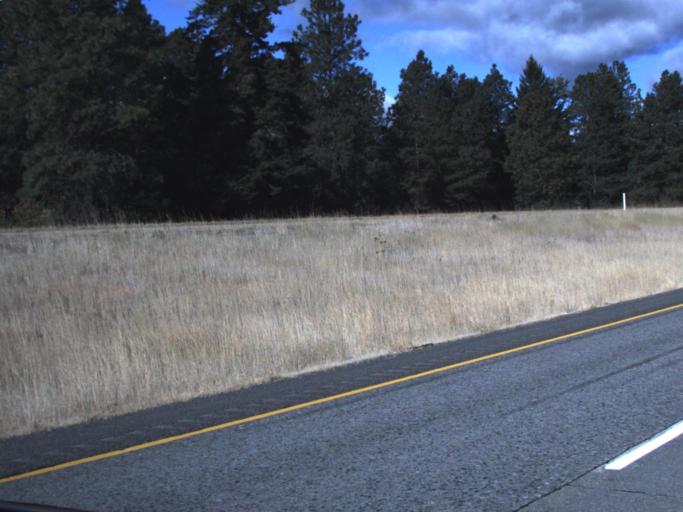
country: US
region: Washington
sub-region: Kittitas County
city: Cle Elum
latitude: 47.2106
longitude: -121.0984
